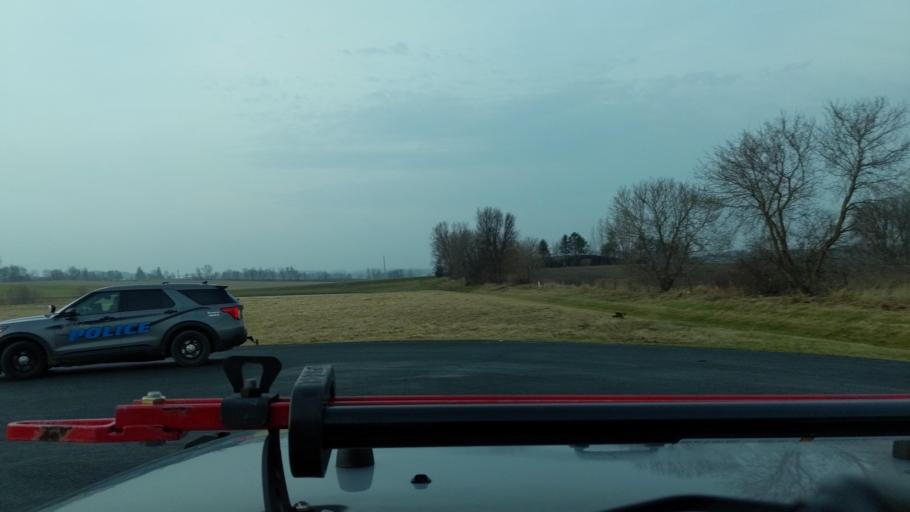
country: US
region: Wisconsin
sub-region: Saint Croix County
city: Baldwin
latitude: 44.9368
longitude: -92.3797
